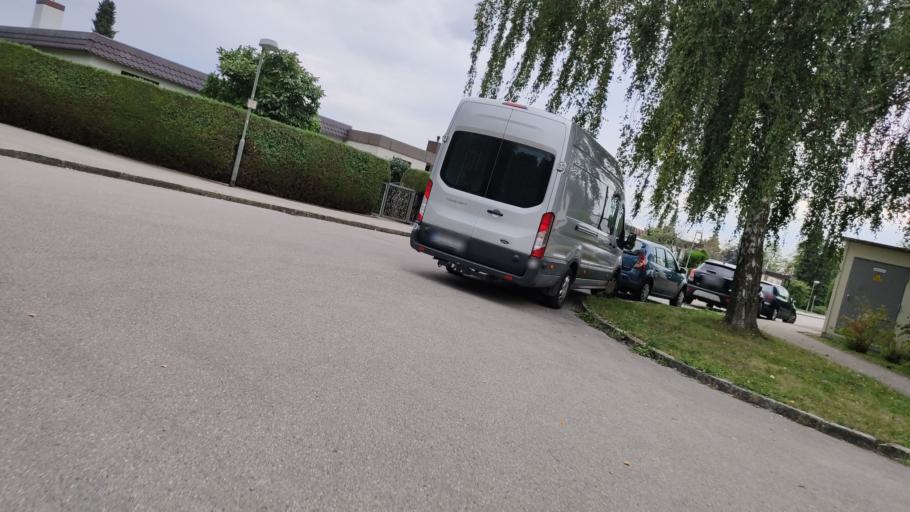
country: DE
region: Bavaria
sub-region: Swabia
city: Konigsbrunn
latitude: 48.2809
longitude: 10.8843
